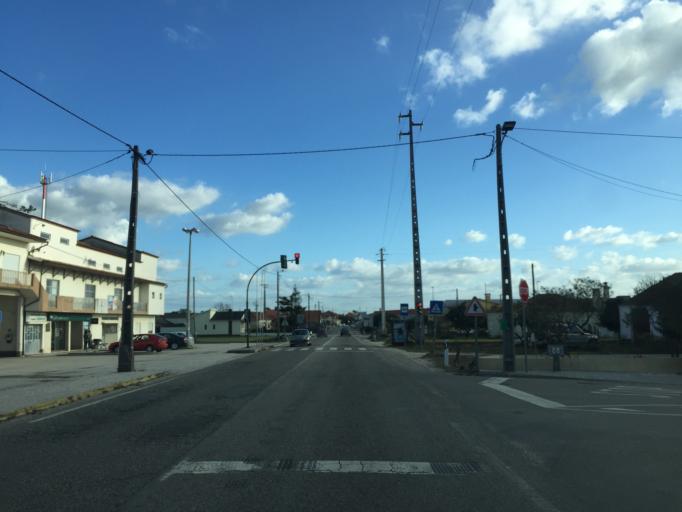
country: PT
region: Leiria
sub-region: Pombal
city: Lourical
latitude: 39.9870
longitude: -8.8008
